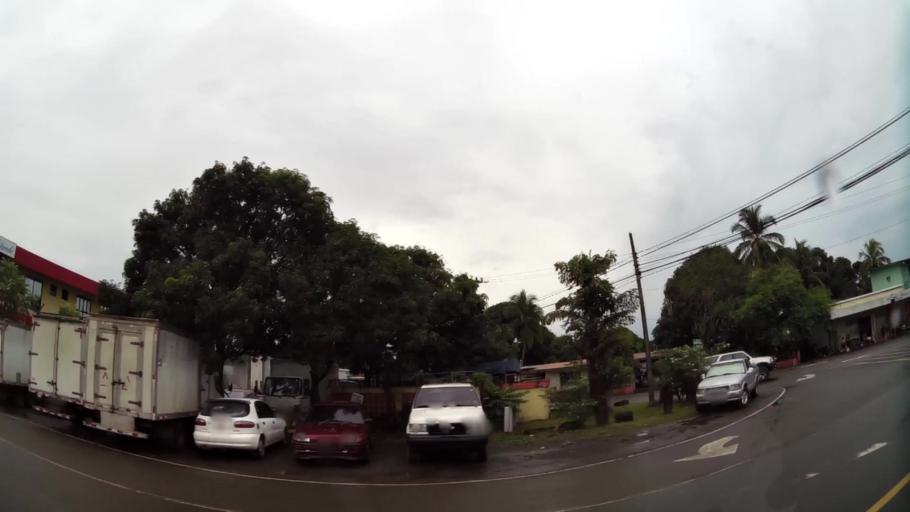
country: PA
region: Veraguas
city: Santiago de Veraguas
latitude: 8.1073
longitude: -80.9748
